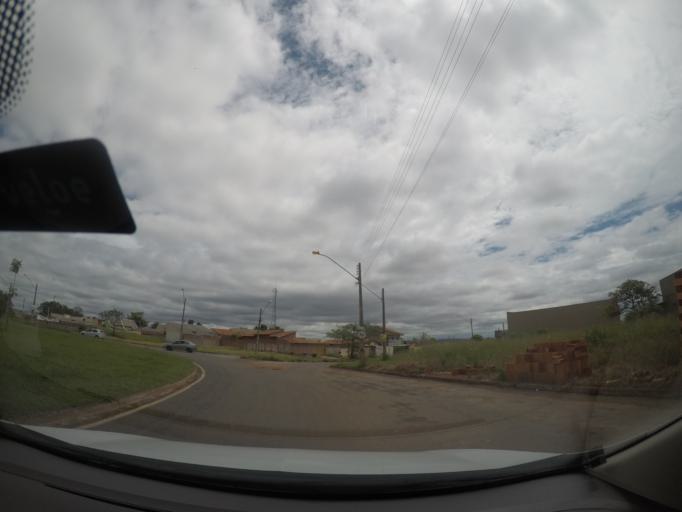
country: BR
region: Goias
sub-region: Goiania
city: Goiania
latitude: -16.7505
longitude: -49.3744
